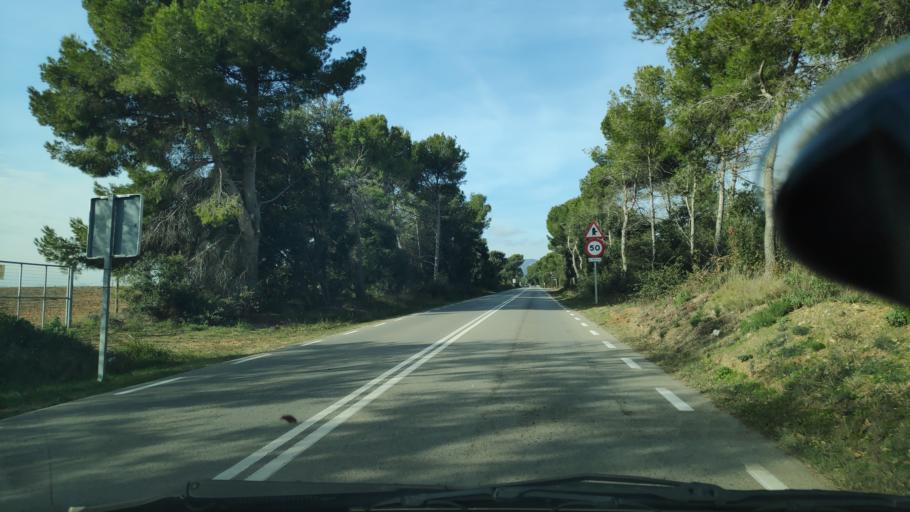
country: ES
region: Catalonia
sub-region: Provincia de Barcelona
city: Matadepera
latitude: 41.5884
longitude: 2.0481
